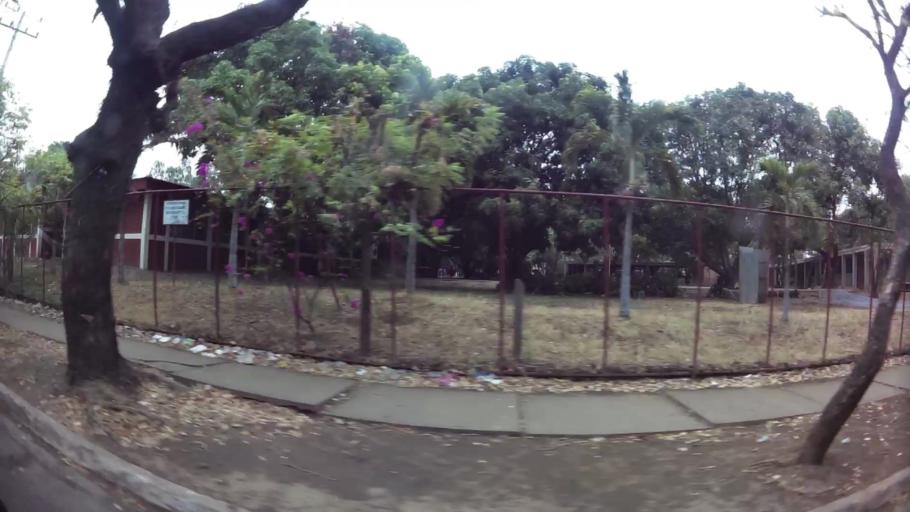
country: NI
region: Leon
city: Leon
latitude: 12.4215
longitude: -86.8756
